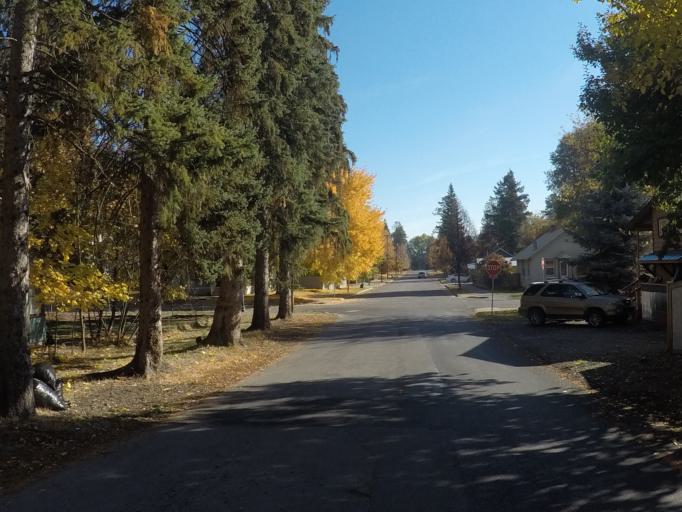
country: US
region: Montana
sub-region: Flathead County
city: Whitefish
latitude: 48.4180
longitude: -114.3471
